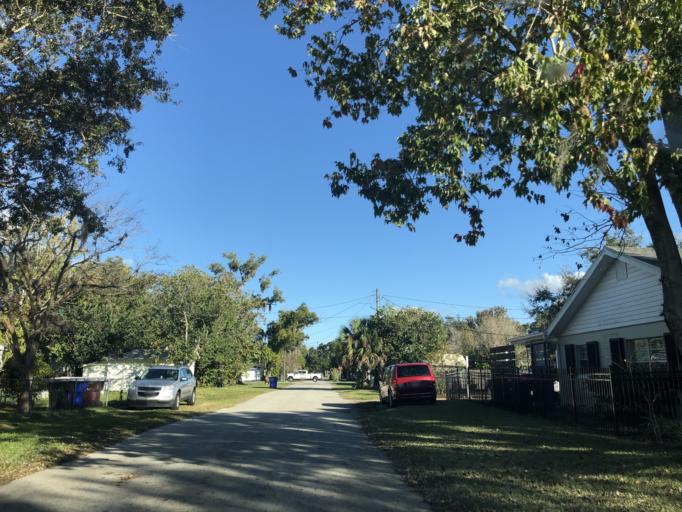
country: US
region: Florida
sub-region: Osceola County
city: Saint Cloud
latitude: 28.2506
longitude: -81.2871
